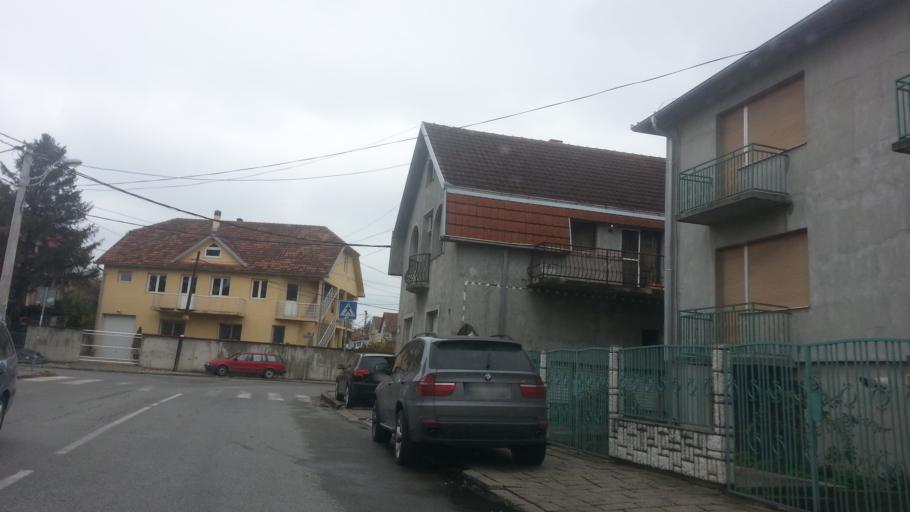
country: RS
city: Novi Banovci
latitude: 44.8993
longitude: 20.2929
